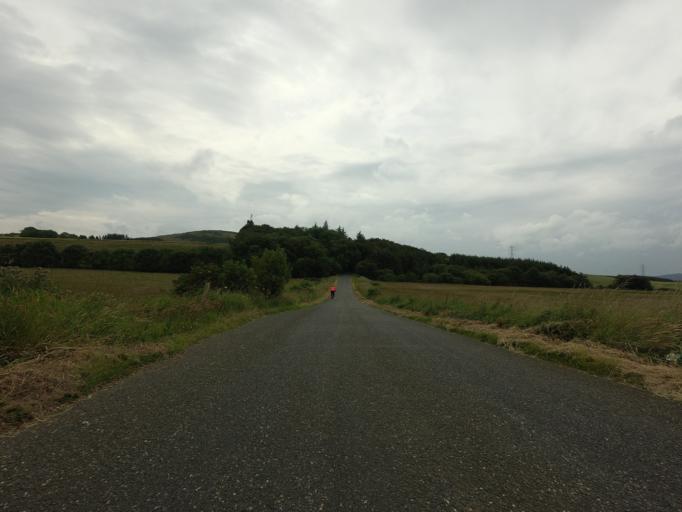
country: GB
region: Scotland
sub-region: Aberdeenshire
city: Portsoy
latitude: 57.6744
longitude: -2.7166
